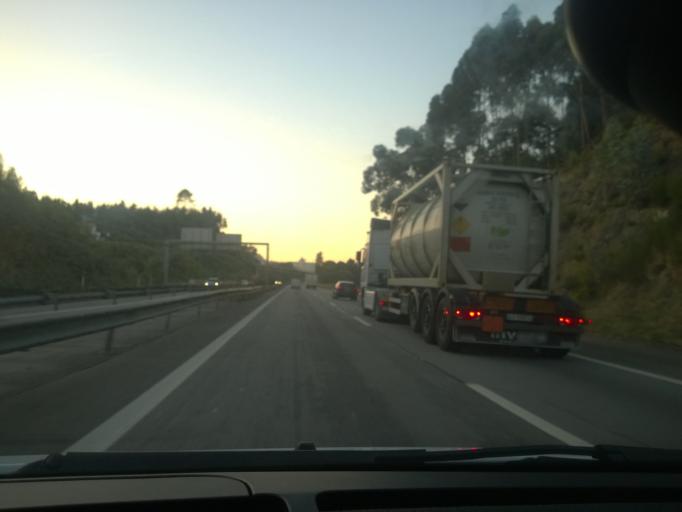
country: PT
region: Porto
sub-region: Vila Nova de Gaia
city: Avintes
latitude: 41.1119
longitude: -8.5679
